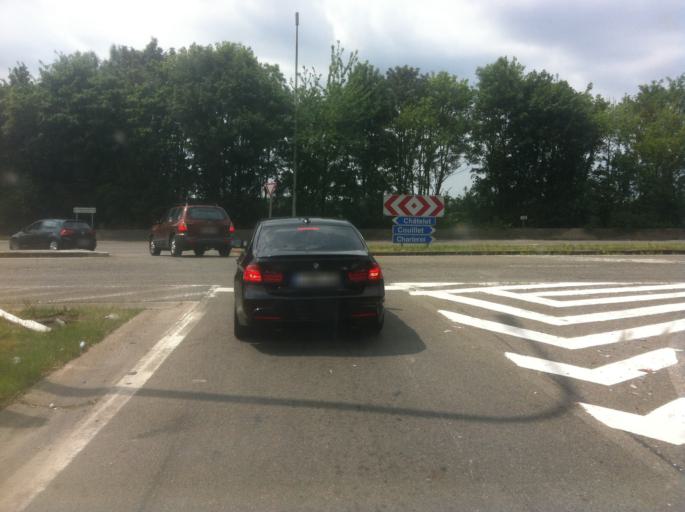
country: BE
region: Wallonia
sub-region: Province du Hainaut
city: Chatelet
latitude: 50.3941
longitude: 4.5080
